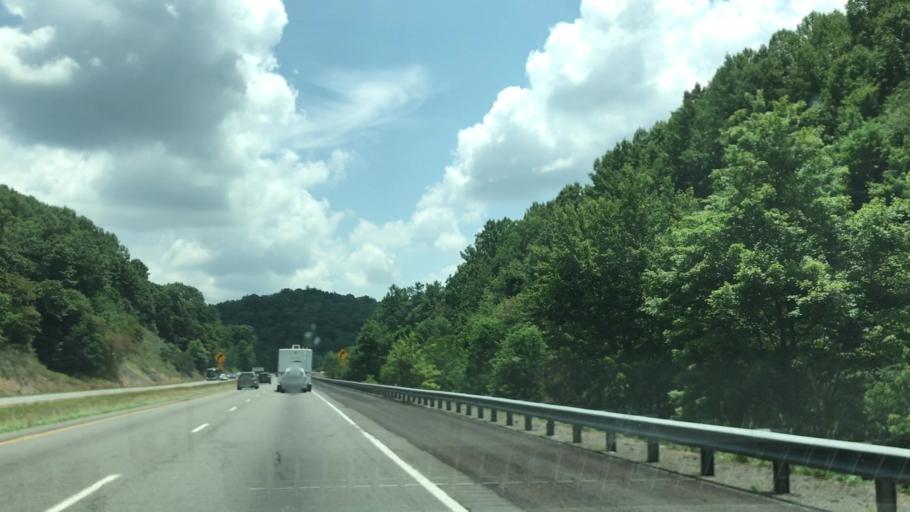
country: US
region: Virginia
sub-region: Carroll County
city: Woodlawn
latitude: 36.8344
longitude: -80.8537
